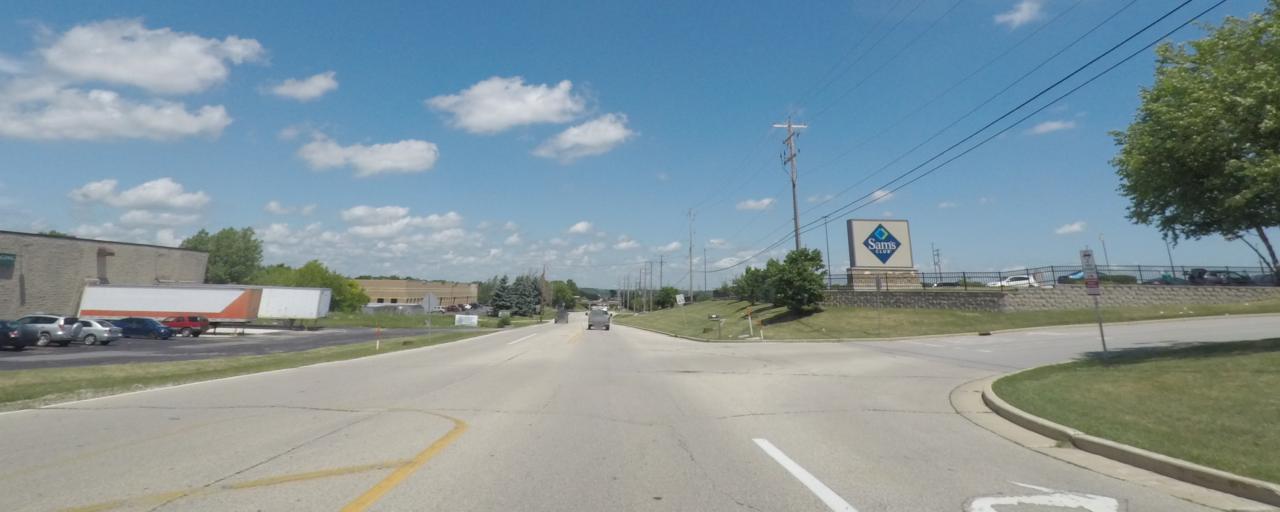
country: US
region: Wisconsin
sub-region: Waukesha County
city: Waukesha
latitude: 43.0376
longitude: -88.1859
